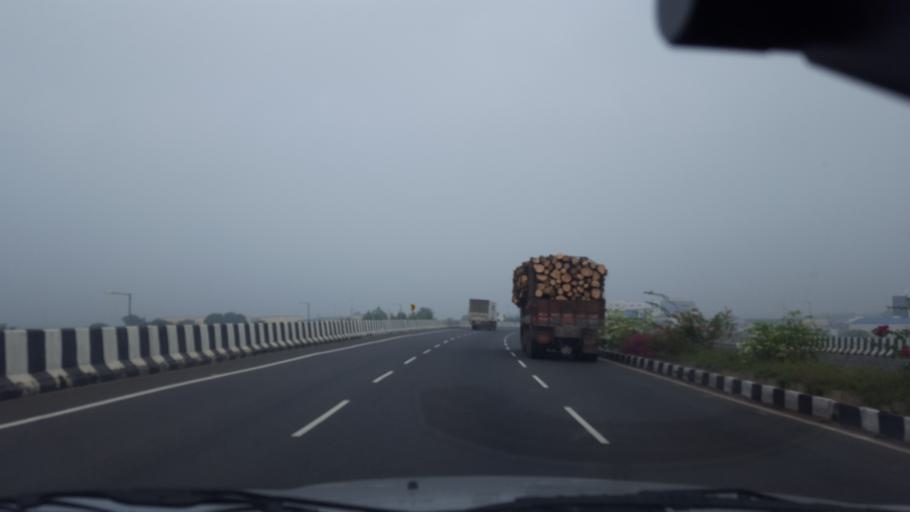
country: IN
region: Andhra Pradesh
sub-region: Prakasam
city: Ongole
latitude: 15.5332
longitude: 80.0517
